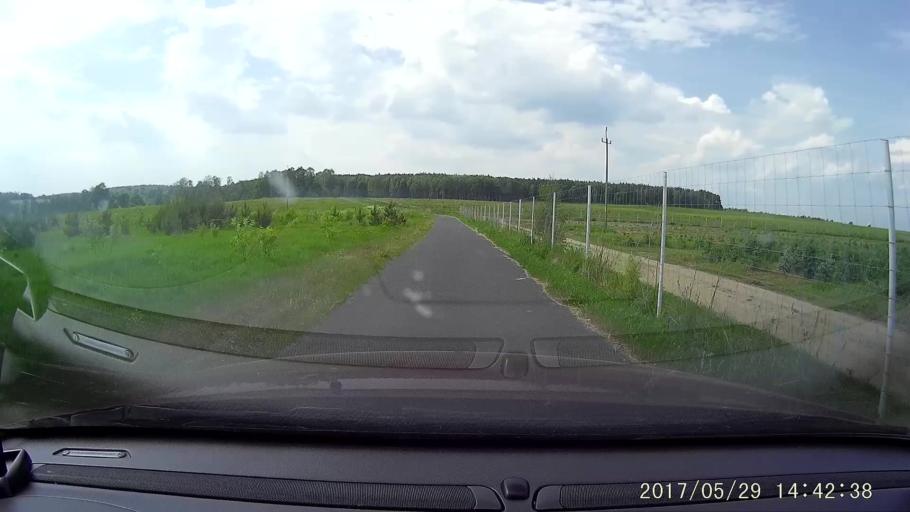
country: PL
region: Lower Silesian Voivodeship
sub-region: Powiat zgorzelecki
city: Wegliniec
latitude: 51.2364
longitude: 15.1987
